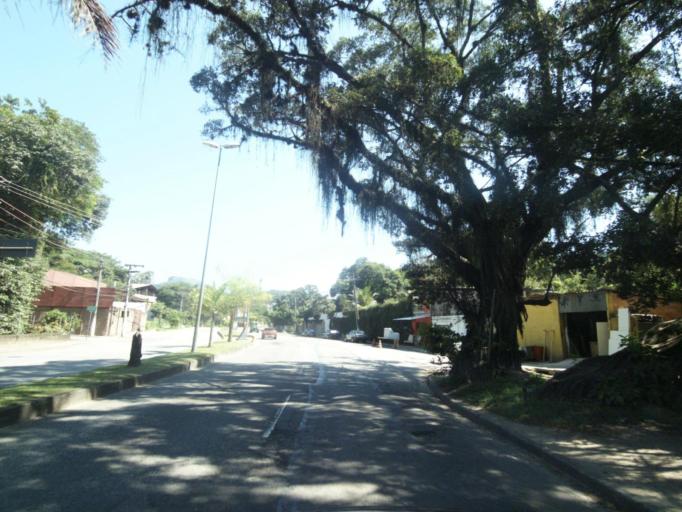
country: BR
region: Rio de Janeiro
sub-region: Niteroi
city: Niteroi
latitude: -22.8949
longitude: -43.0382
